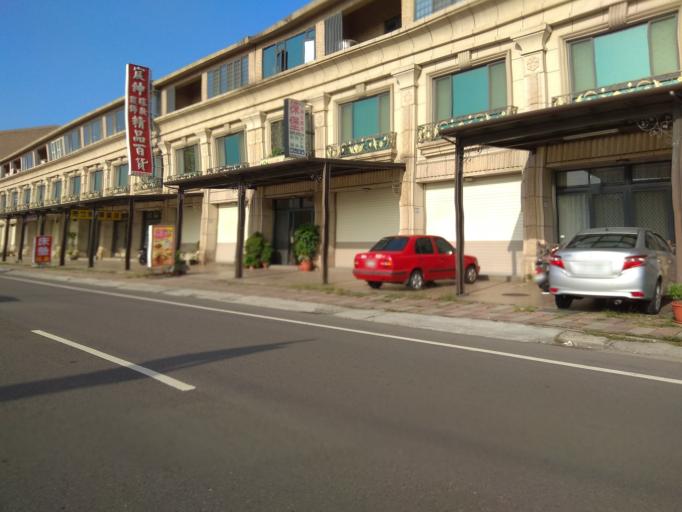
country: TW
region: Taiwan
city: Taoyuan City
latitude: 24.9636
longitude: 121.1474
